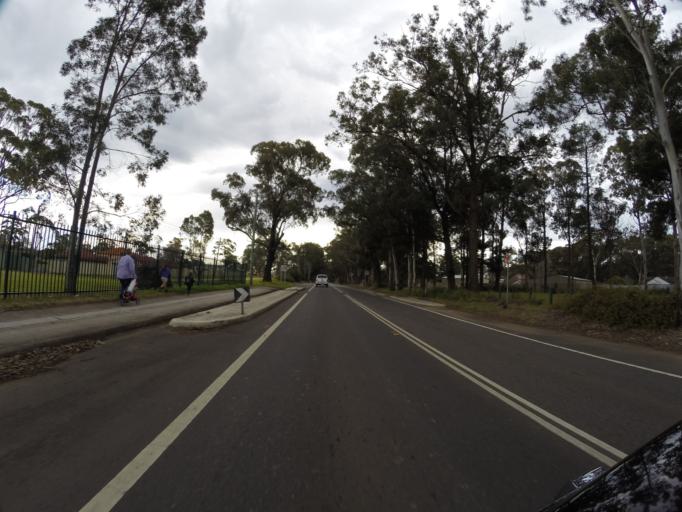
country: AU
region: New South Wales
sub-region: Wollondilly
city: Douglas Park
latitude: -34.1975
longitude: 150.7887
